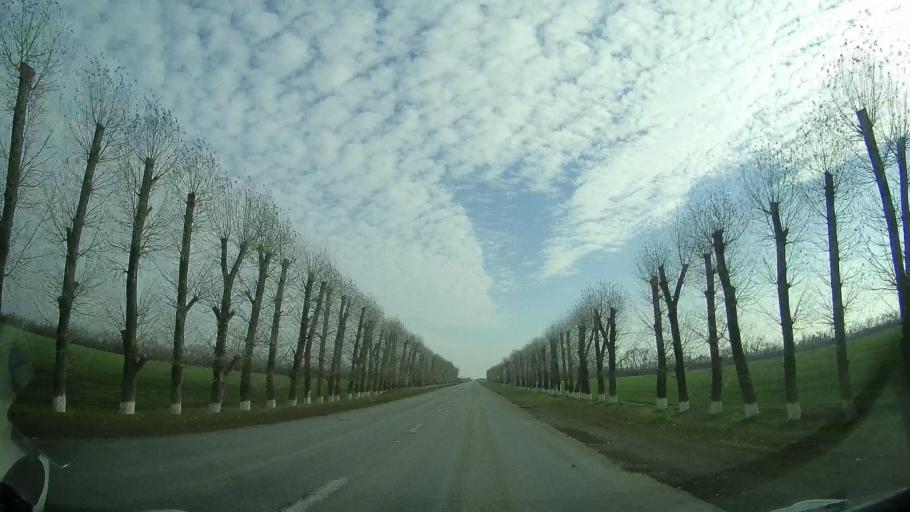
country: RU
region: Rostov
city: Tselina
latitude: 46.5279
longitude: 41.0613
